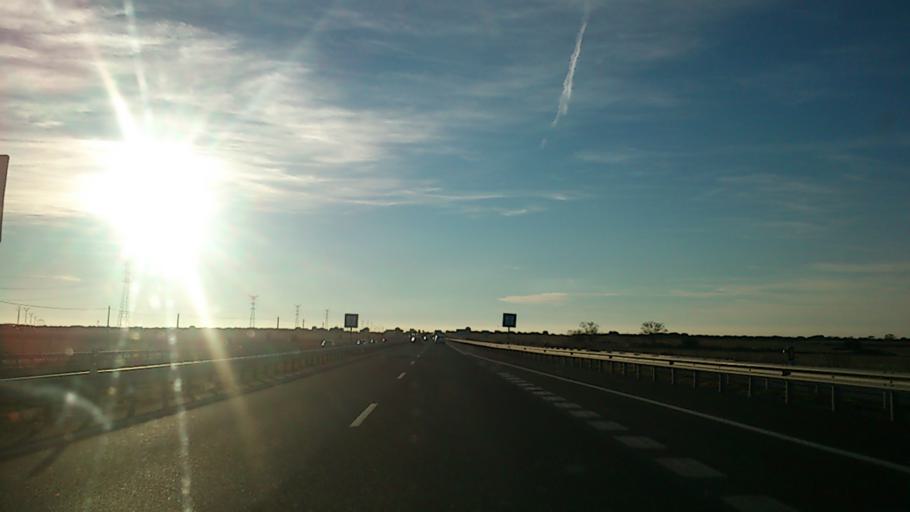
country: ES
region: Castille-La Mancha
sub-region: Provincia de Guadalajara
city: Ledanca
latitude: 40.8549
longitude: -2.8469
